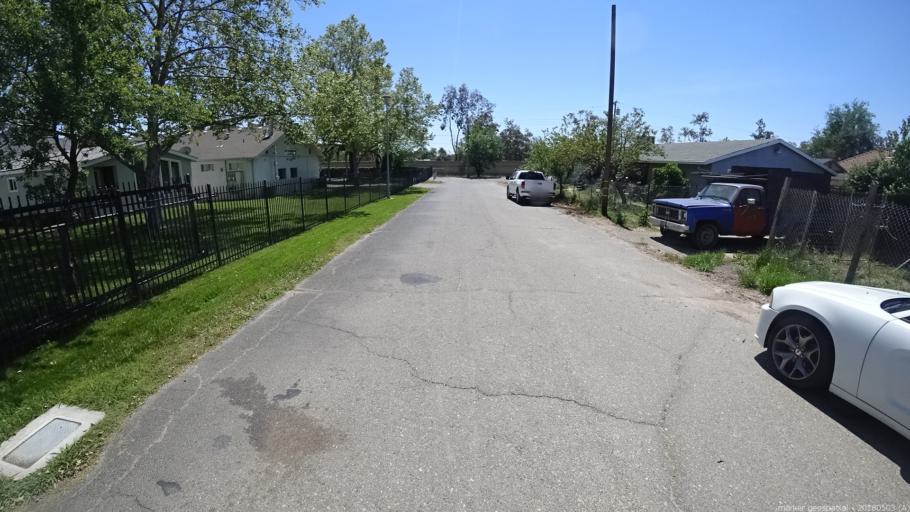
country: US
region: California
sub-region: Sacramento County
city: Rio Linda
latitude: 38.6443
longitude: -121.4304
